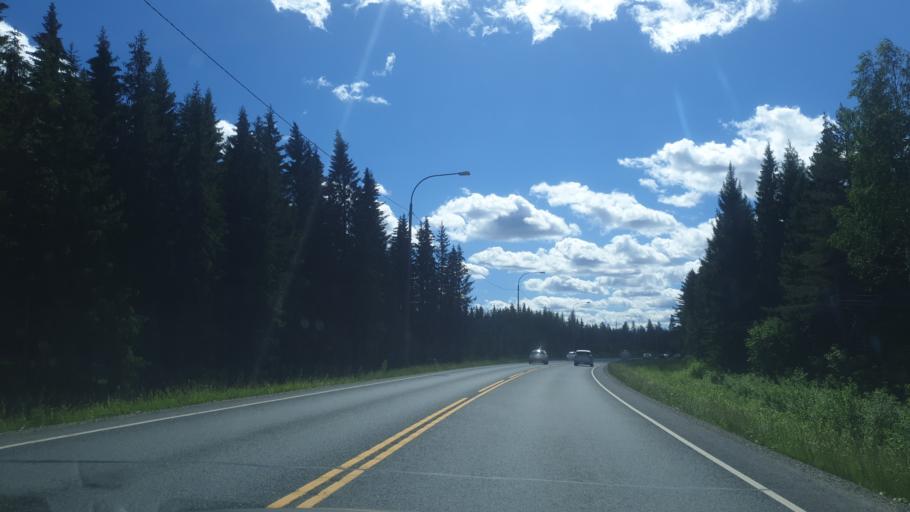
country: FI
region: Northern Savo
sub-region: Varkaus
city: Leppaevirta
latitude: 62.5637
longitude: 27.6209
